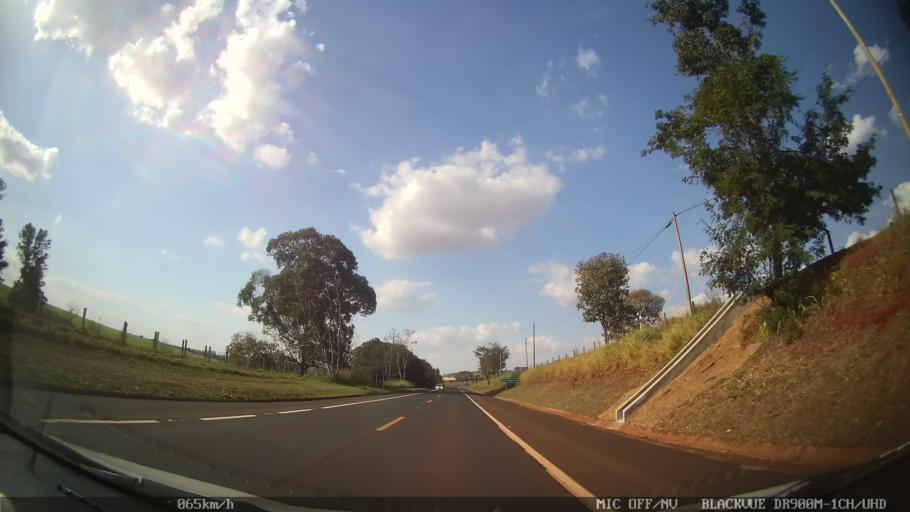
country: BR
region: Sao Paulo
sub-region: Ribeirao Preto
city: Ribeirao Preto
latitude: -21.1941
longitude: -47.8709
